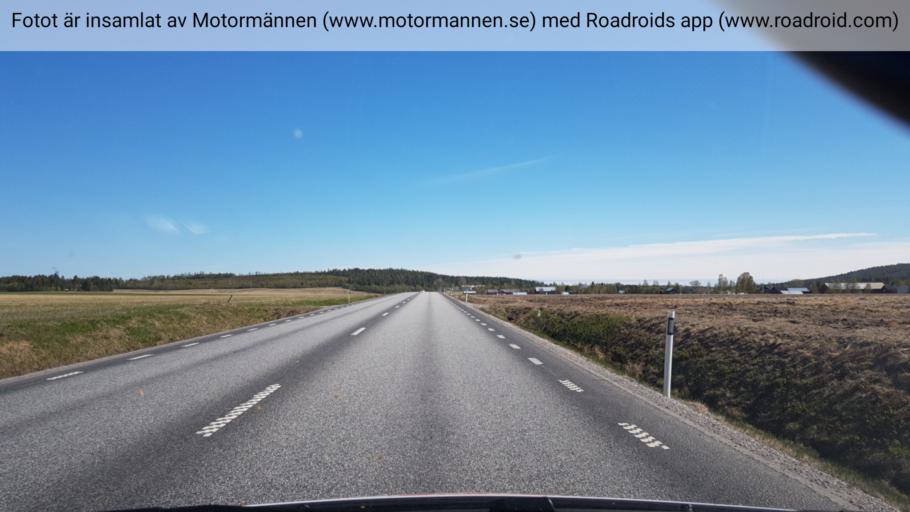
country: SE
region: Vaesterbotten
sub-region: Umea Kommun
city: Roback
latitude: 63.8723
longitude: 20.0695
